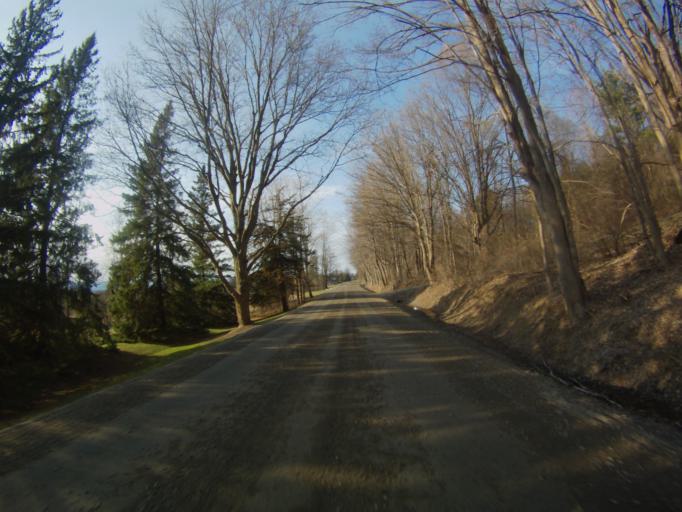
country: US
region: Vermont
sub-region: Addison County
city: Vergennes
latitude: 44.0588
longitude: -73.2928
